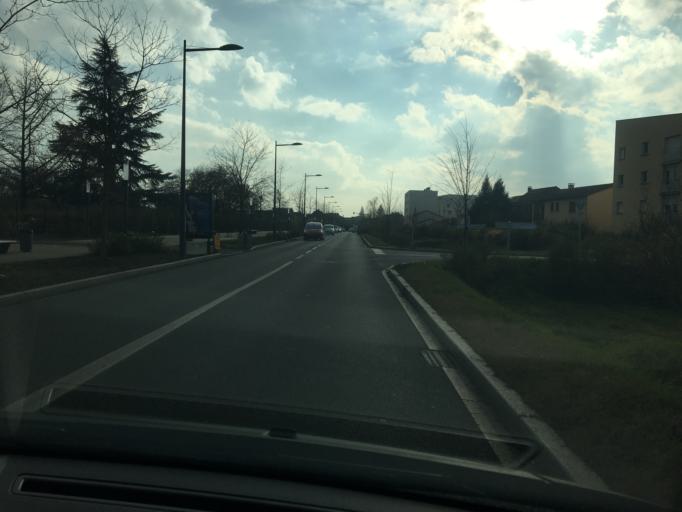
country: FR
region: Auvergne
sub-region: Departement de l'Allier
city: Cusset
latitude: 46.1310
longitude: 3.4359
